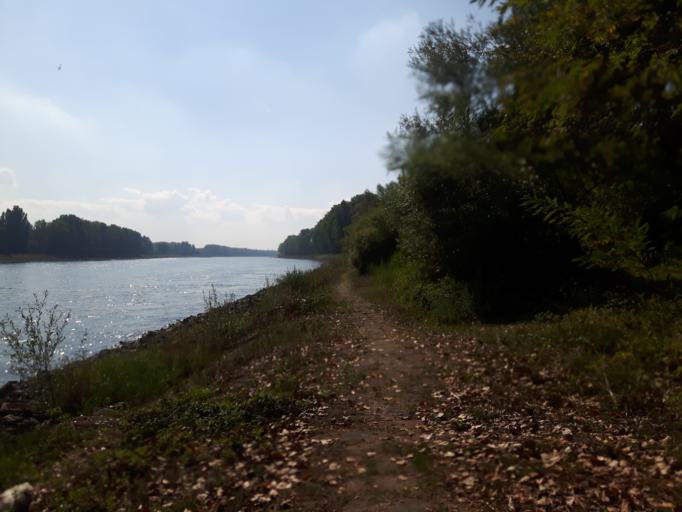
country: DE
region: Rheinland-Pfalz
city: Altrip
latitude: 49.4039
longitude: 8.4946
